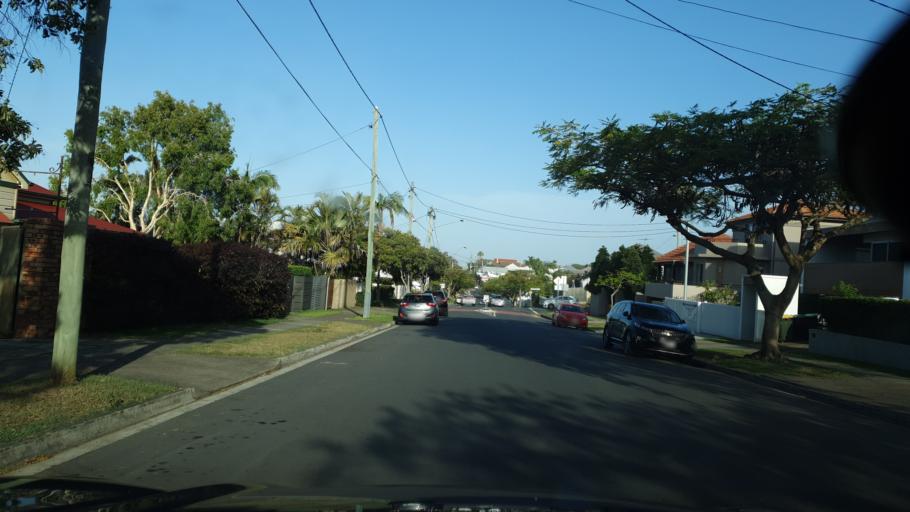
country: AU
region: Queensland
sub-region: Brisbane
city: Ascot
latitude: -27.4298
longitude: 153.0549
